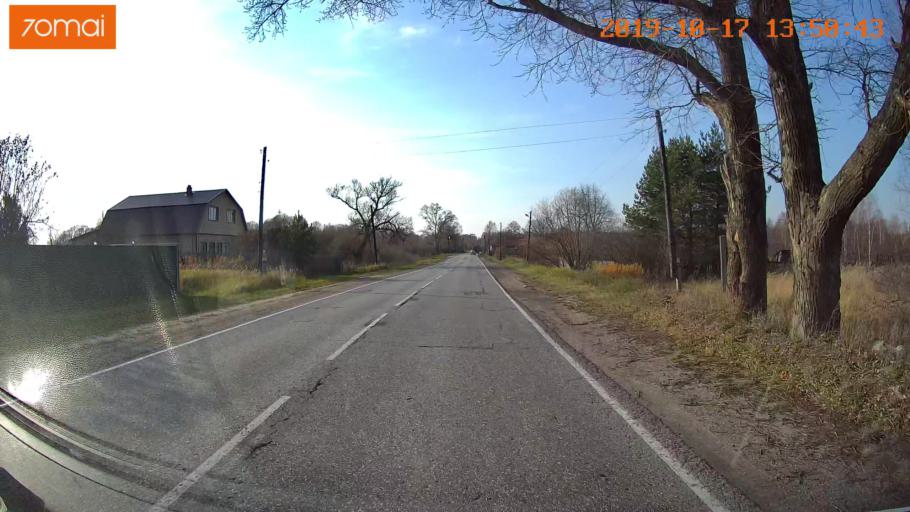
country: RU
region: Rjazan
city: Tuma
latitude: 55.1401
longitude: 40.4014
